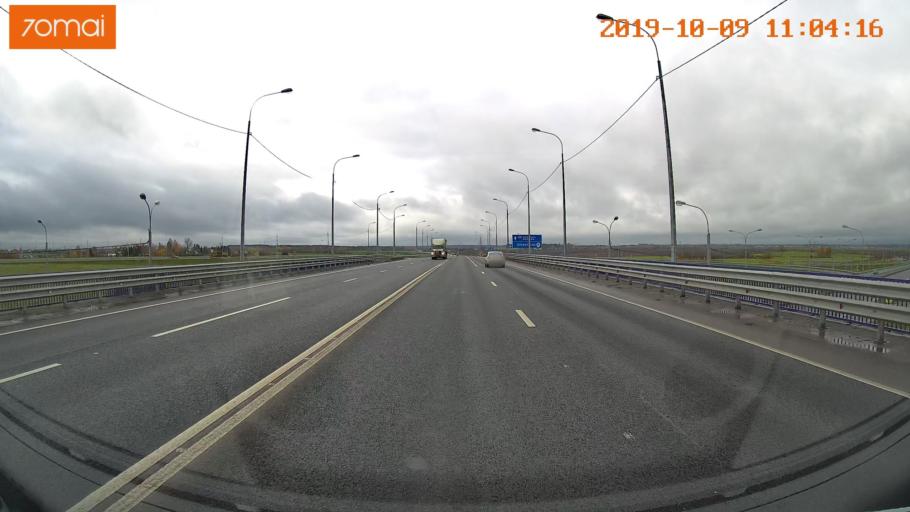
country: RU
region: Vologda
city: Vologda
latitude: 59.2138
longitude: 39.7692
